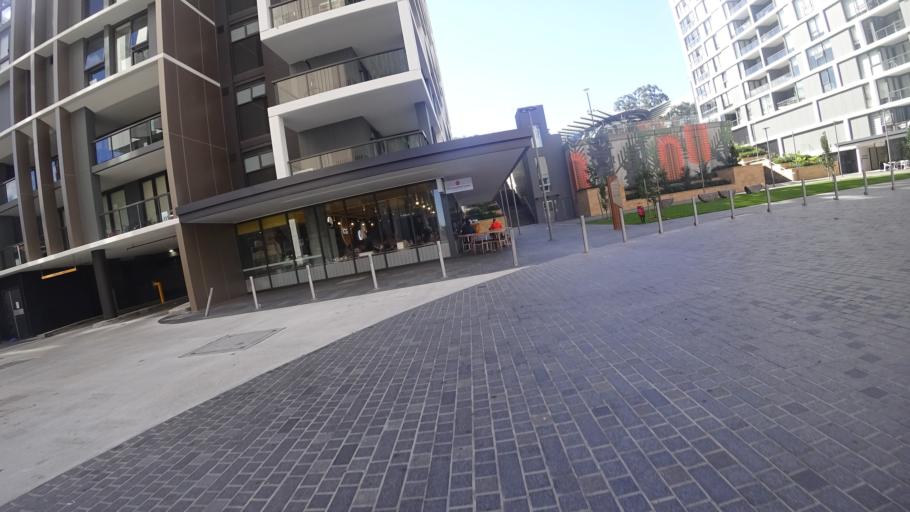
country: AU
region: New South Wales
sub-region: Ryde
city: North Ryde
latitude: -33.7952
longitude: 151.1380
